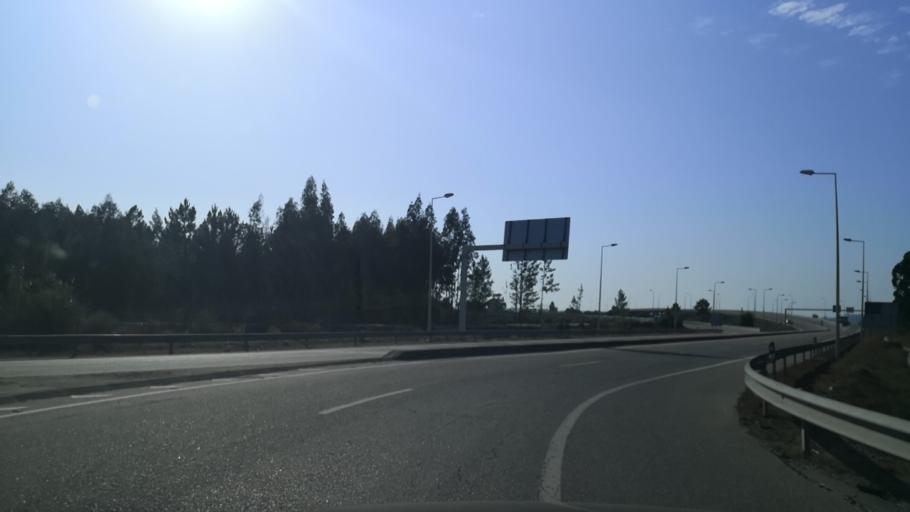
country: PT
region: Santarem
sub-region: Almeirim
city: Almeirim
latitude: 39.1746
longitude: -8.6224
